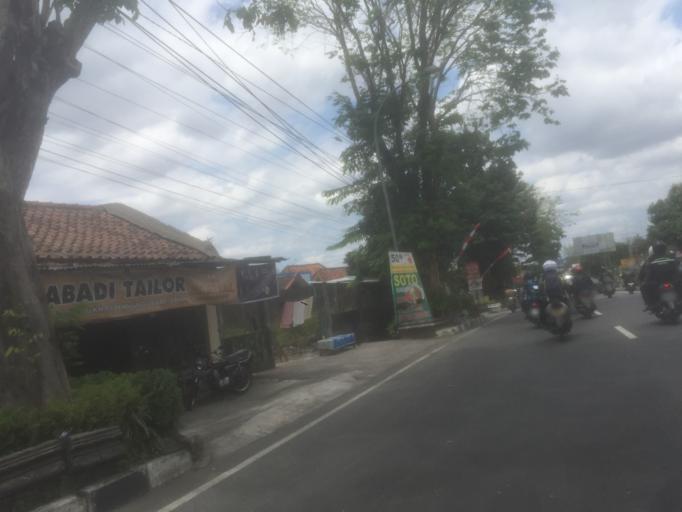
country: ID
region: Daerah Istimewa Yogyakarta
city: Sleman
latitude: -7.7223
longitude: 110.3616
